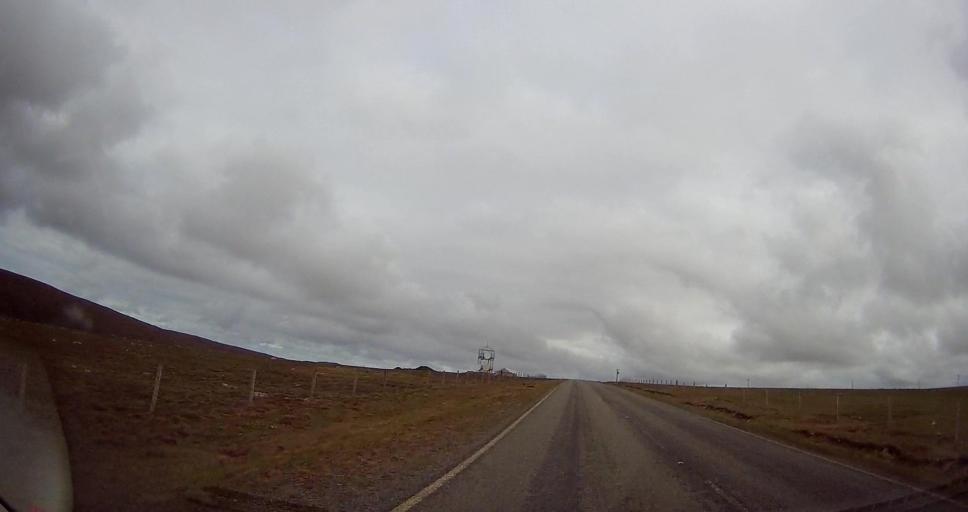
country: GB
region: Scotland
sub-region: Shetland Islands
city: Shetland
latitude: 60.7349
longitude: -0.8947
